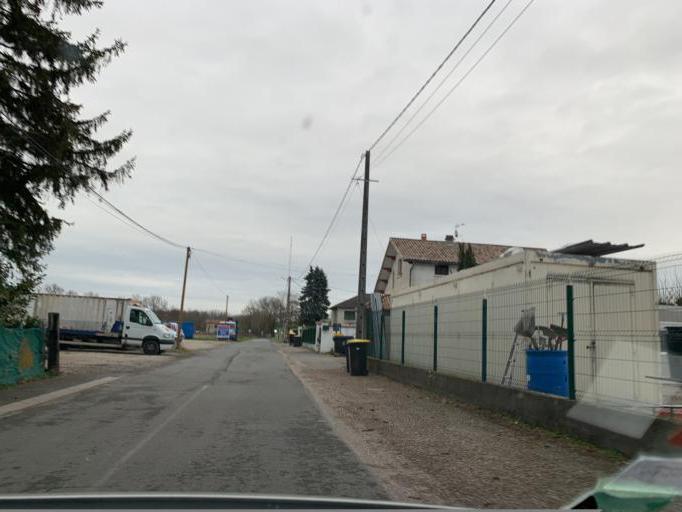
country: FR
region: Rhone-Alpes
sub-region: Departement de l'Ain
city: Mionnay
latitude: 45.8733
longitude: 4.9344
